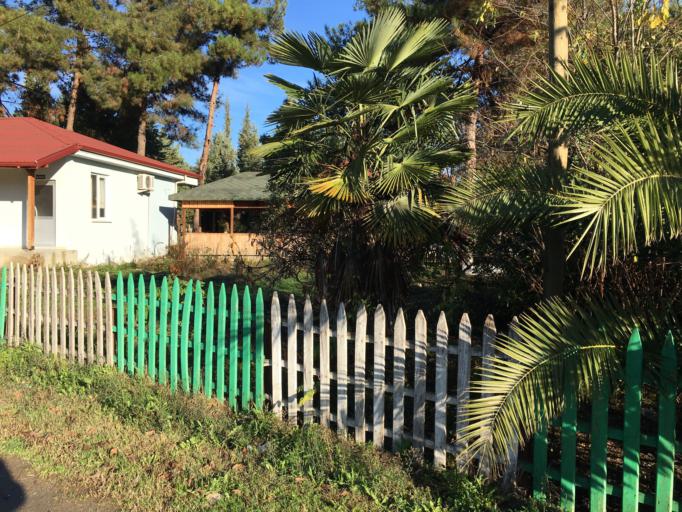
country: TR
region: Samsun
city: Alacam
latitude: 41.6136
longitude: 35.6032
